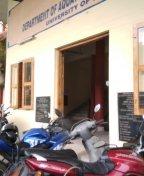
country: IN
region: Kerala
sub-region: Thiruvananthapuram
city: Thiruvananthapuram
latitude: 8.5627
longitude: 76.8883
